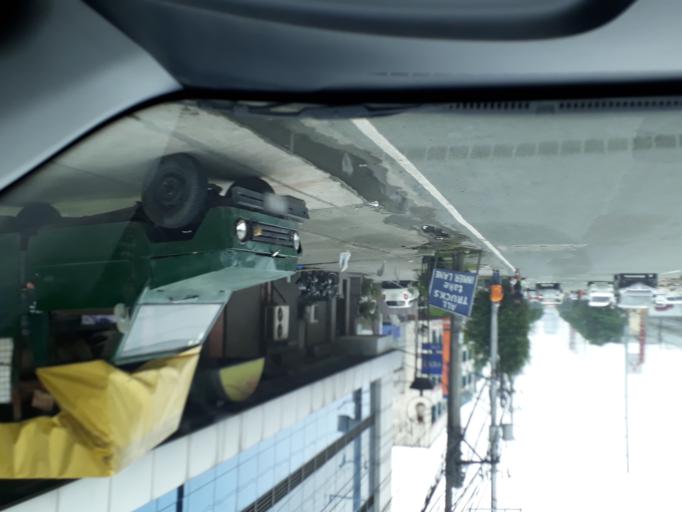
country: PH
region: Metro Manila
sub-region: City of Manila
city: Quiapo
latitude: 14.5905
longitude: 120.9981
